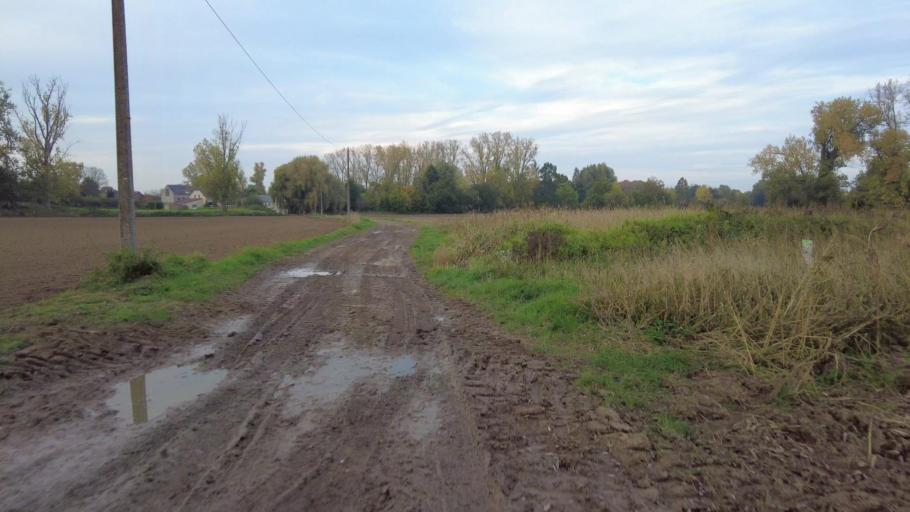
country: BE
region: Wallonia
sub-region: Province du Brabant Wallon
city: Jodoigne
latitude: 50.7395
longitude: 4.8747
